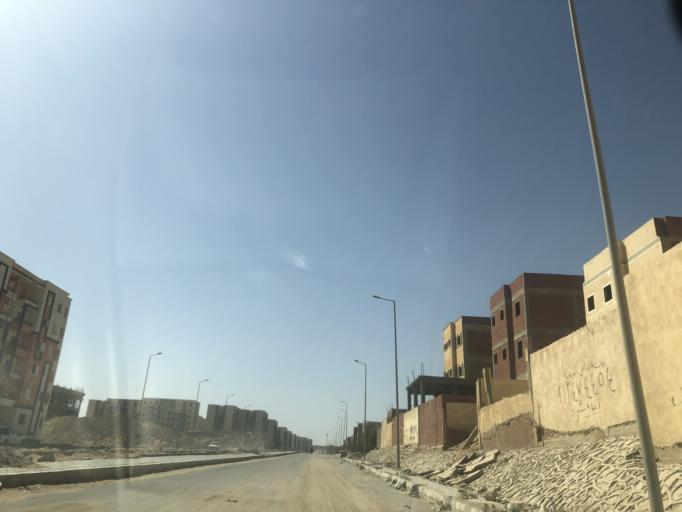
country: EG
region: Al Jizah
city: Madinat Sittah Uktubar
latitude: 29.9276
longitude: 30.9941
